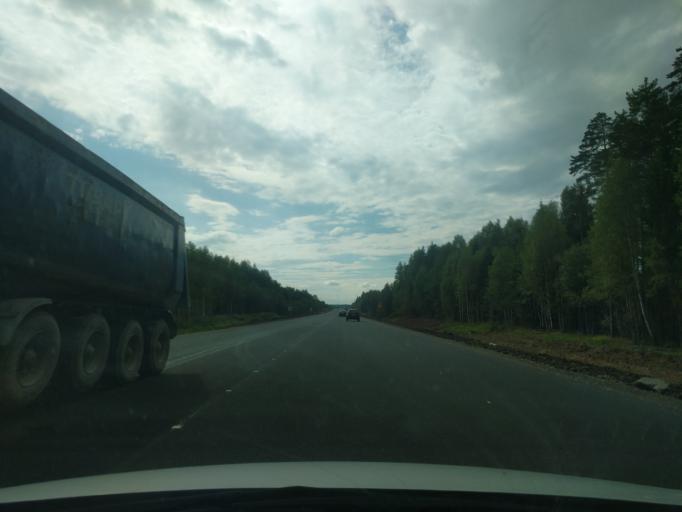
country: RU
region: Kostroma
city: Sudislavl'
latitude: 57.8206
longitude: 41.4895
